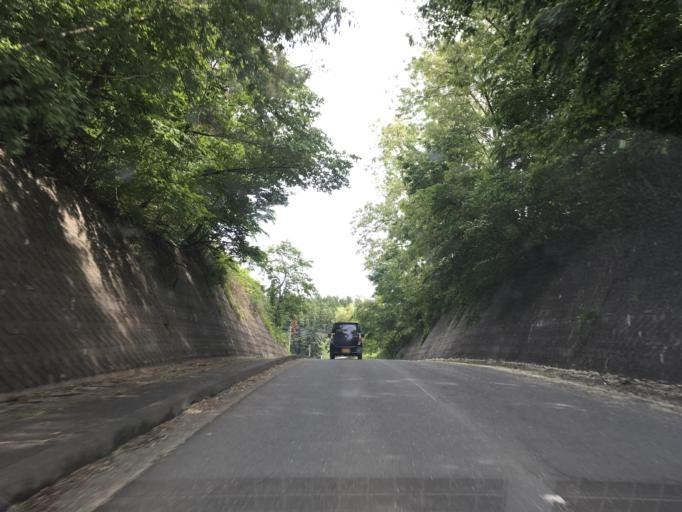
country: JP
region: Iwate
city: Mizusawa
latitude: 39.0652
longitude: 141.3578
